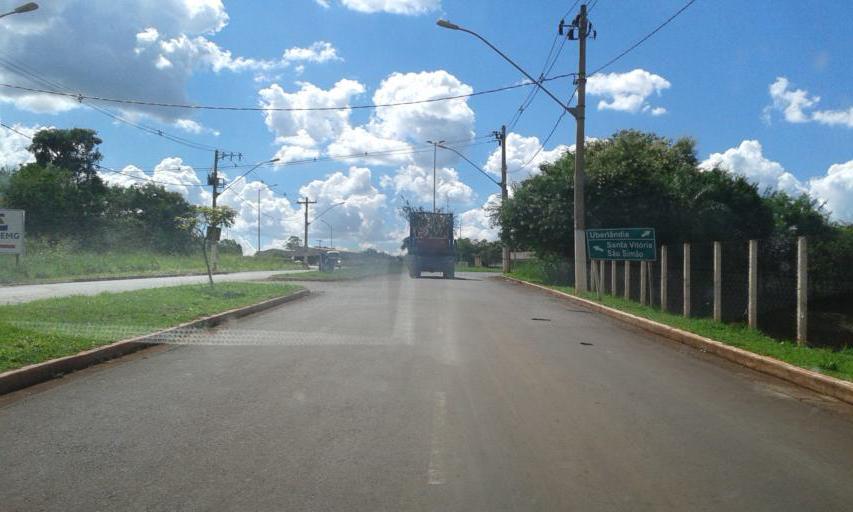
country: BR
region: Minas Gerais
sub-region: Ituiutaba
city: Ituiutaba
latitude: -18.9671
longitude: -49.4901
